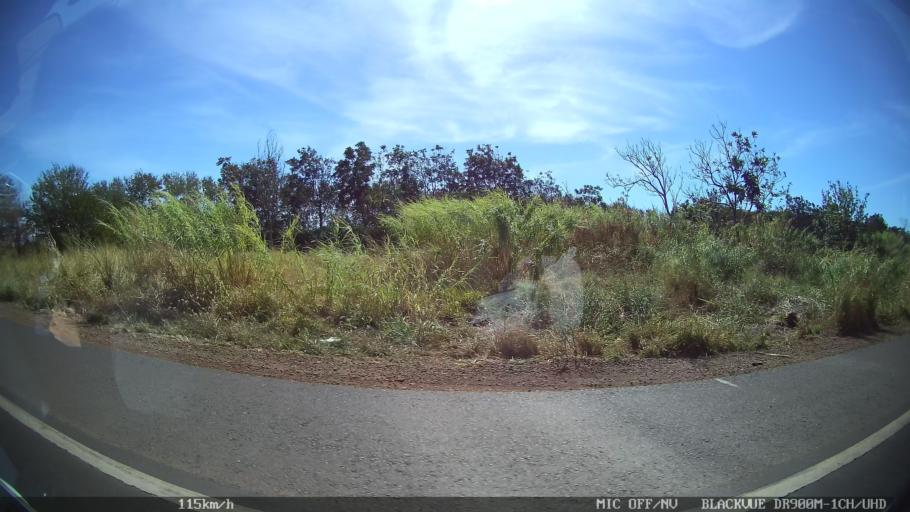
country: BR
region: Sao Paulo
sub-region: Franca
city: Franca
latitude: -20.5569
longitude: -47.5922
